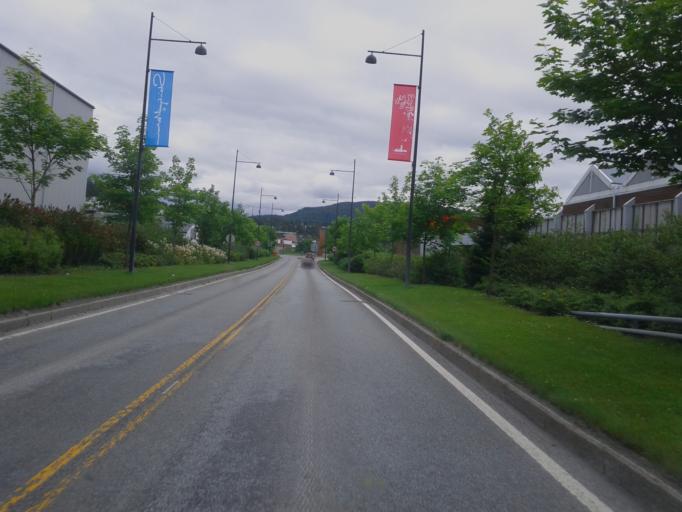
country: NO
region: Nord-Trondelag
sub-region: Steinkjer
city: Steinkjer
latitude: 64.0224
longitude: 11.4882
